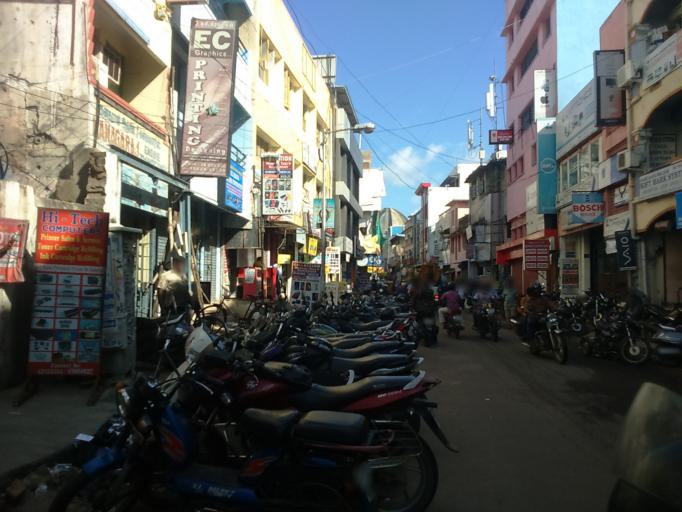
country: IN
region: Tamil Nadu
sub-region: Chennai
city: Chennai
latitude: 13.0703
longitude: 80.2699
